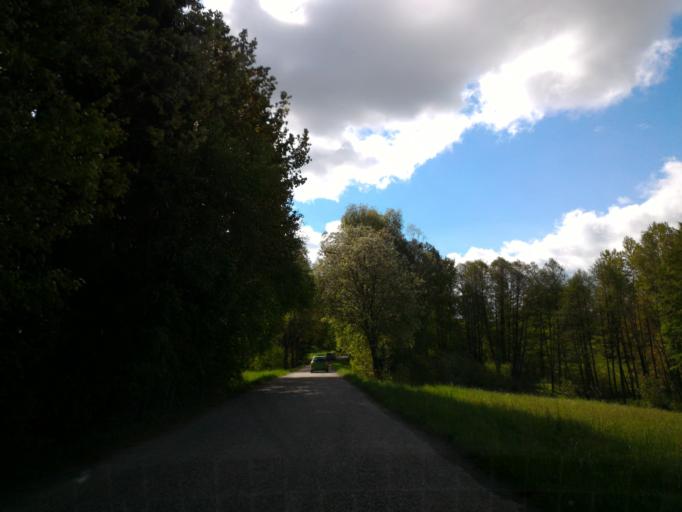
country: CZ
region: Vysocina
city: Ledec nad Sazavou
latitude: 49.6312
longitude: 15.3065
